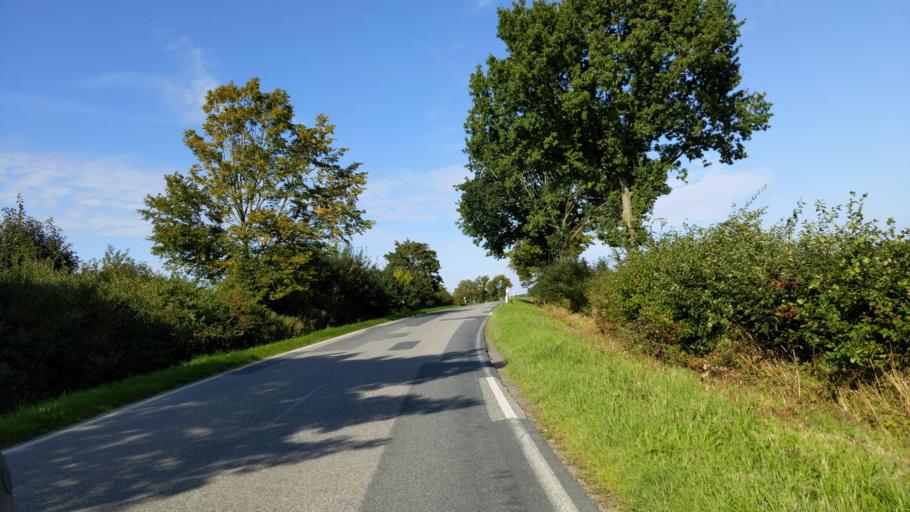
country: DE
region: Schleswig-Holstein
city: Bad Schwartau
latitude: 53.9747
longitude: 10.6554
